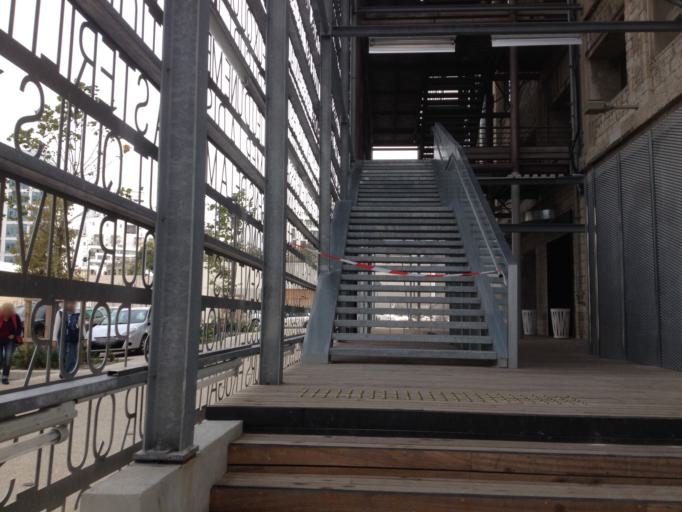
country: FR
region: Provence-Alpes-Cote d'Azur
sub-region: Departement des Bouches-du-Rhone
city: Marseille 03
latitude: 43.3090
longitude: 5.3667
